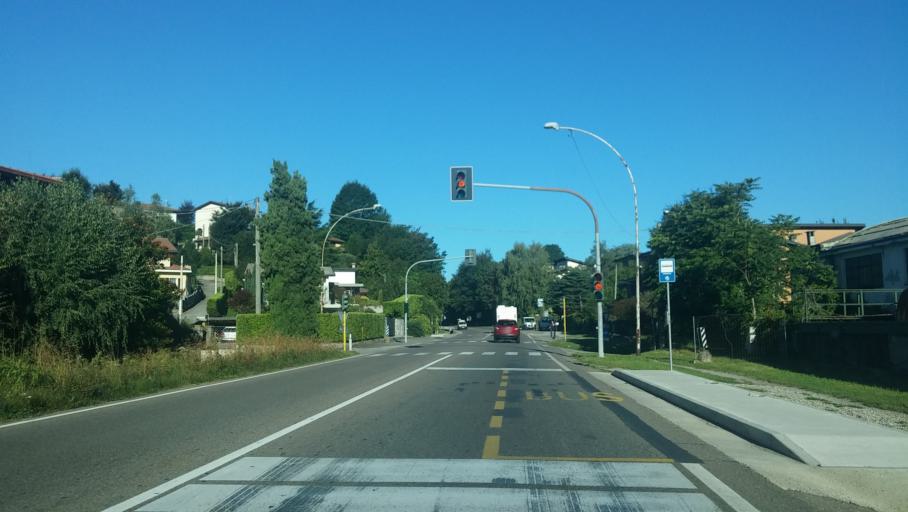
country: IT
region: Lombardy
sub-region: Provincia di Como
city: Albese Con Cassano
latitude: 45.7943
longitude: 9.1634
